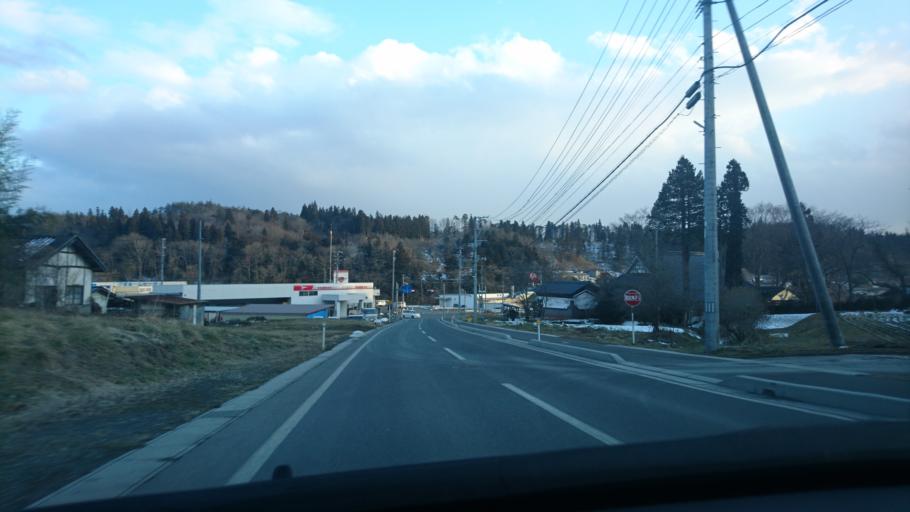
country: JP
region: Iwate
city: Ichinoseki
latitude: 38.9993
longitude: 141.3335
